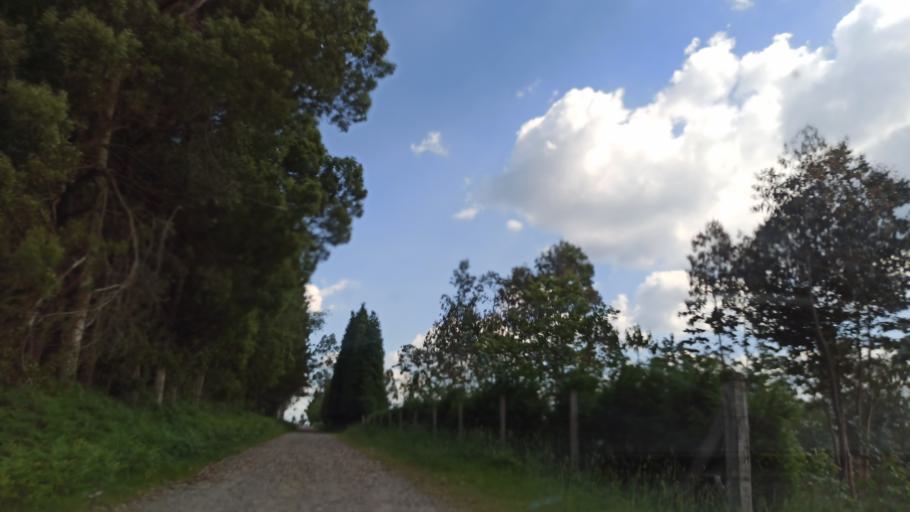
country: ES
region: Galicia
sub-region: Provincia da Coruna
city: Santa Comba
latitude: 43.0772
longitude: -8.7177
